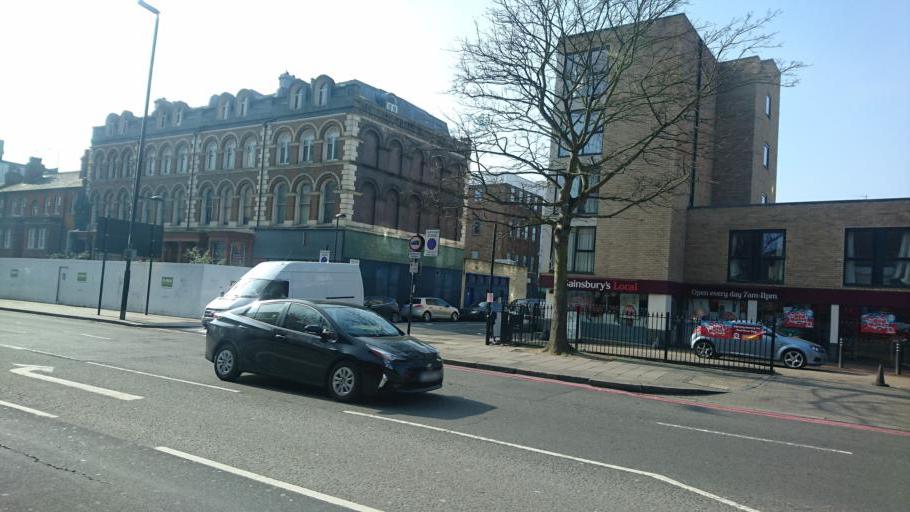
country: GB
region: England
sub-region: Greater London
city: Holloway
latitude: 51.5603
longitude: -0.1229
